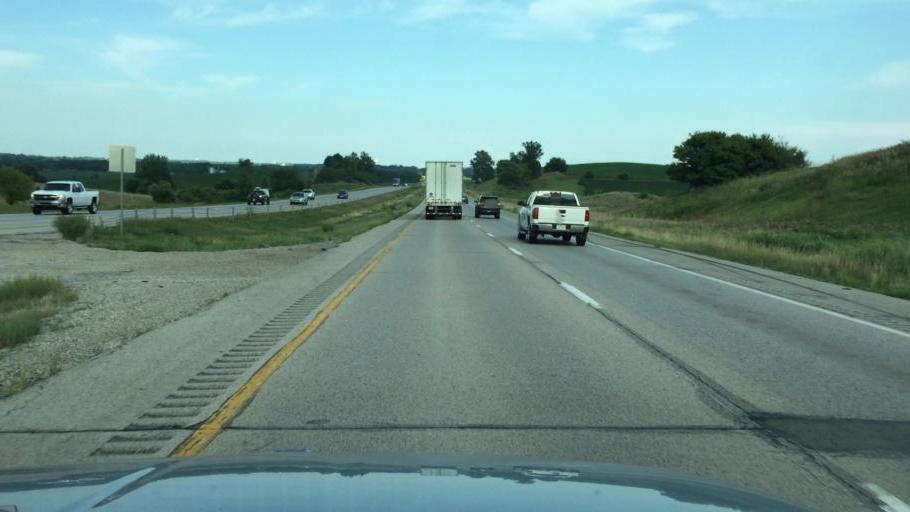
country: US
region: Iowa
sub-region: Johnson County
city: Tiffin
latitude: 41.6952
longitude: -91.7149
